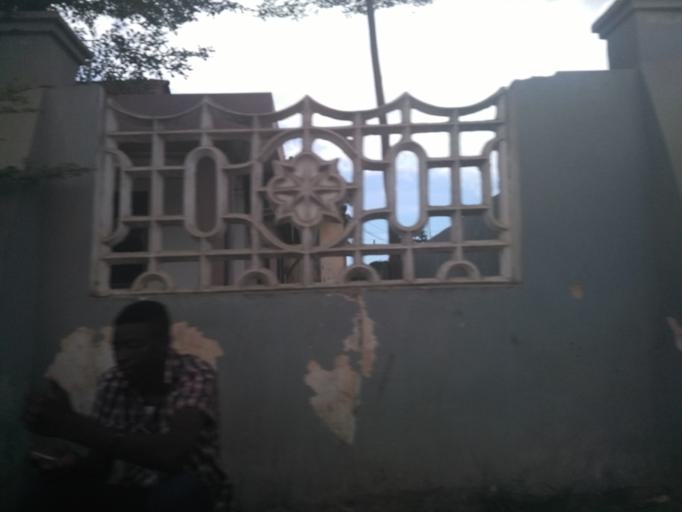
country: TZ
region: Dar es Salaam
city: Magomeni
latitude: -6.7799
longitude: 39.2646
